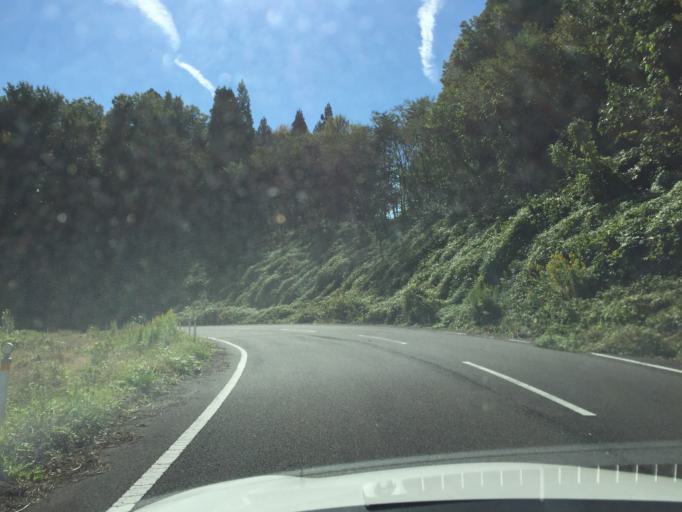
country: JP
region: Fukushima
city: Funehikimachi-funehiki
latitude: 37.4235
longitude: 140.5475
